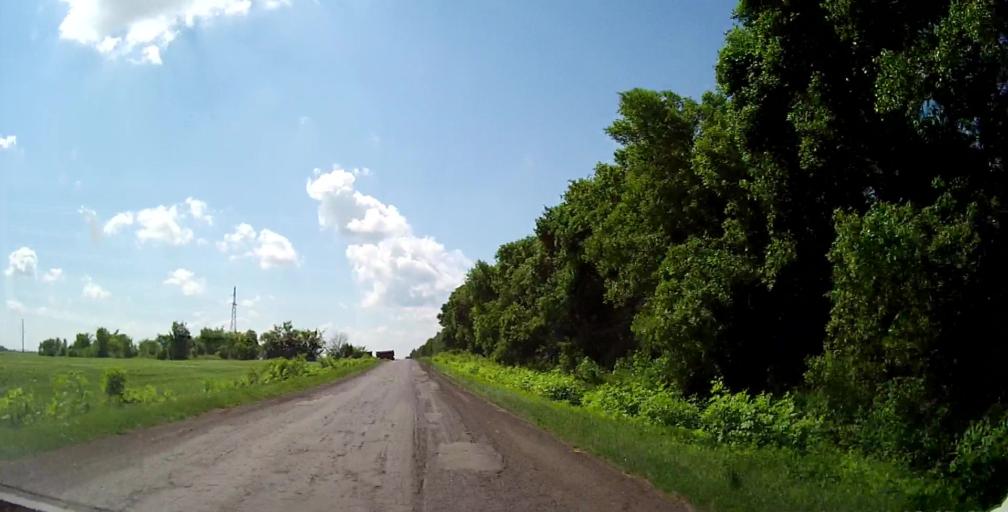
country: RU
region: Lipetsk
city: Chaplygin
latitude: 53.2941
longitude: 39.9562
